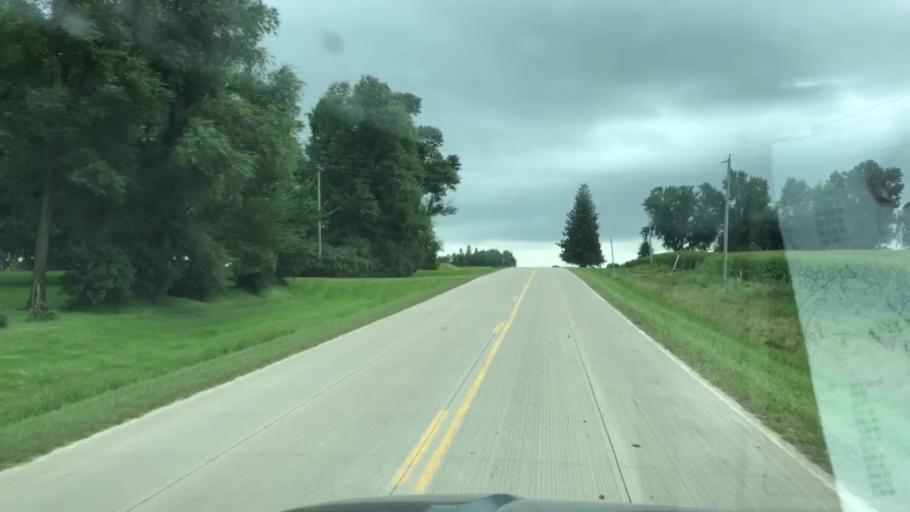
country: US
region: Iowa
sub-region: Sioux County
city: Alton
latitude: 43.1104
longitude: -95.9787
